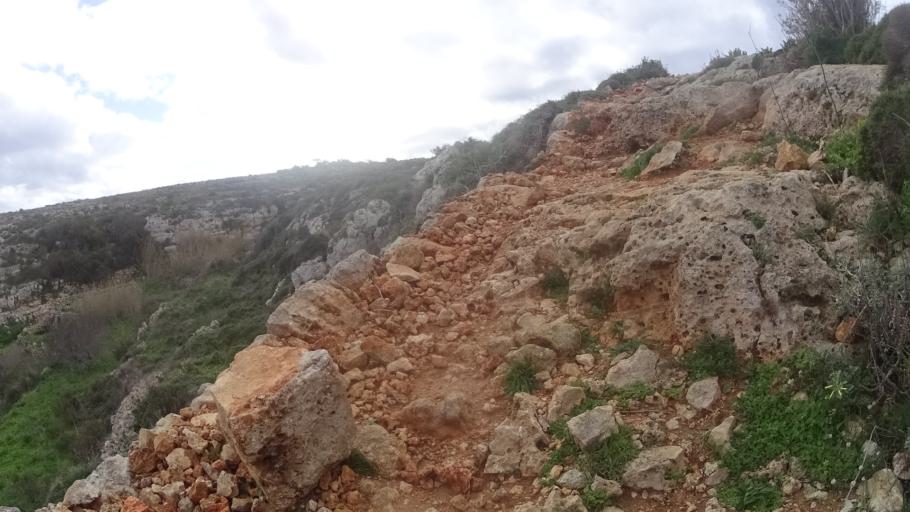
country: MT
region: Il-Mellieha
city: Mellieha
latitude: 35.9753
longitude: 14.3264
